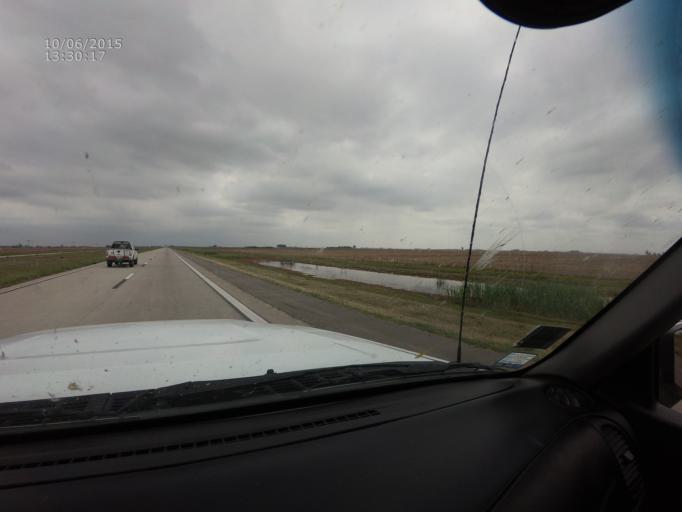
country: AR
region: Cordoba
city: Leones
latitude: -32.6353
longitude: -62.2615
